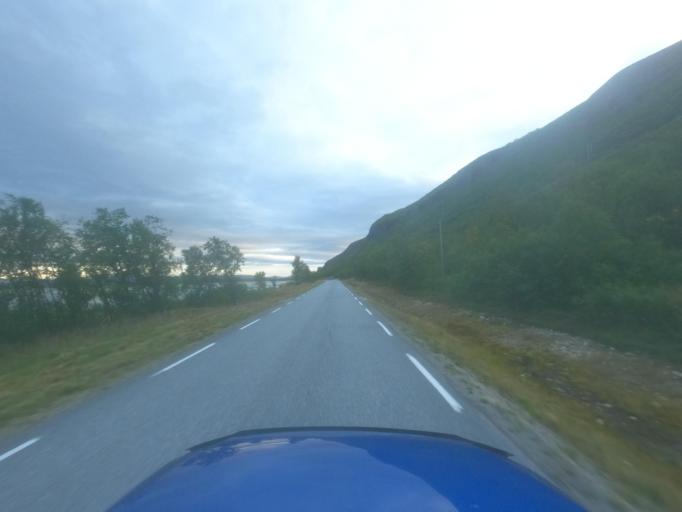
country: NO
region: Finnmark Fylke
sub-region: Porsanger
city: Lakselv
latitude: 70.0980
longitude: 24.9117
